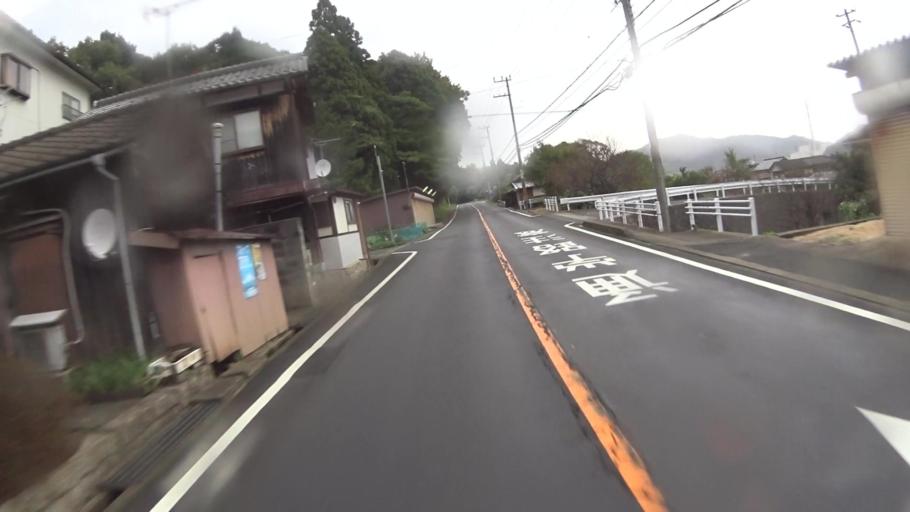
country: JP
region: Kyoto
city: Miyazu
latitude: 35.5558
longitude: 135.2365
